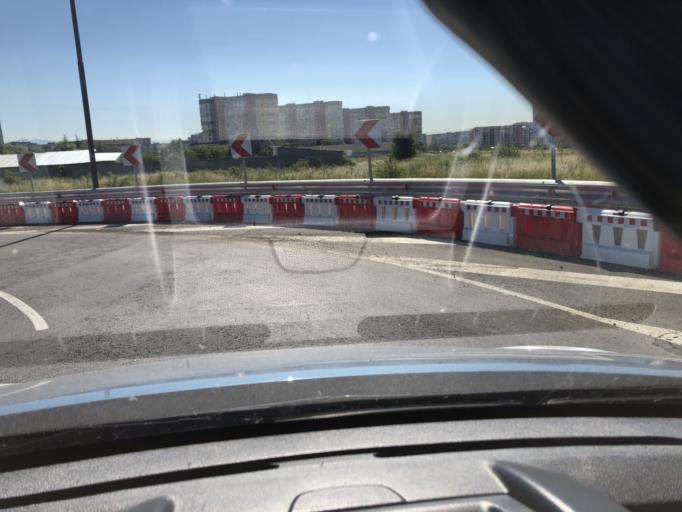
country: BG
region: Sofiya
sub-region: Obshtina Bozhurishte
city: Bozhurishte
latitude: 42.7124
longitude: 23.2361
